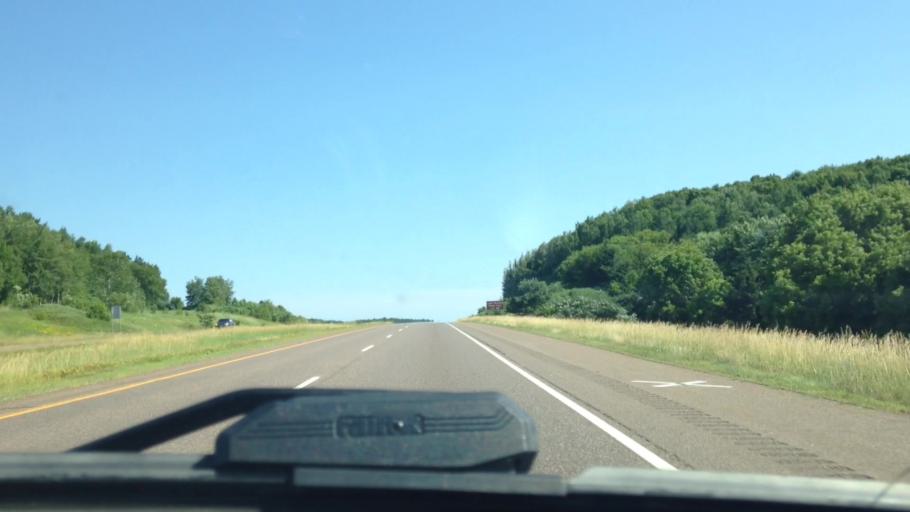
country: US
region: Wisconsin
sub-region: Chippewa County
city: Chippewa Falls
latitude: 44.9522
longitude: -91.4260
